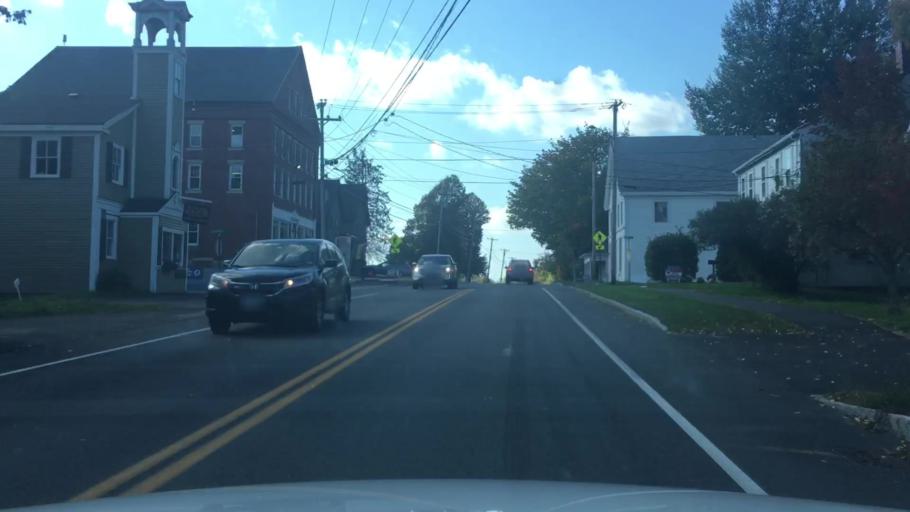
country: US
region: Maine
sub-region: Knox County
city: Thomaston
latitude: 44.0779
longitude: -69.1909
